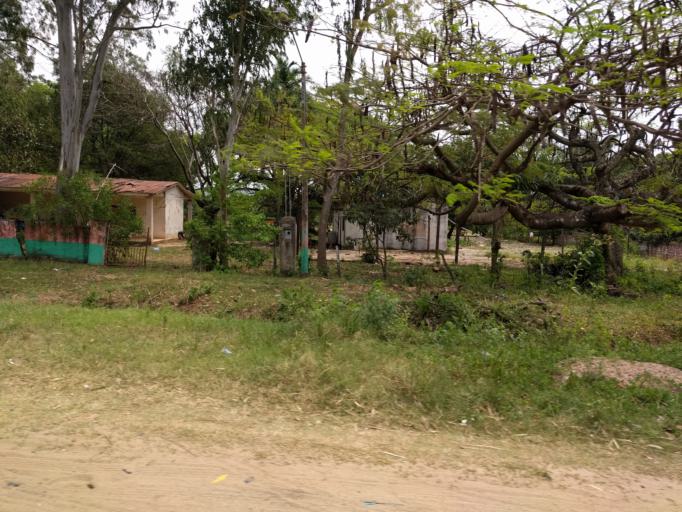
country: BO
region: Santa Cruz
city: Santa Rita
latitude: -17.9138
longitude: -63.3454
